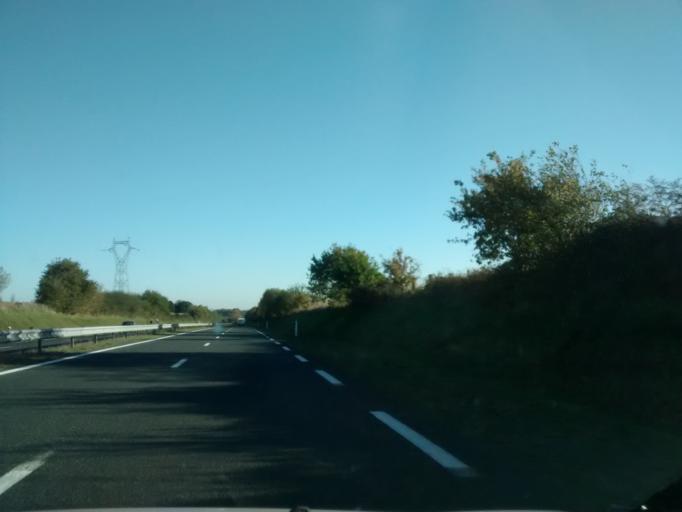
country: FR
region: Brittany
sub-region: Departement des Cotes-d'Armor
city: Pedernec
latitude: 48.5793
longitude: -3.2298
